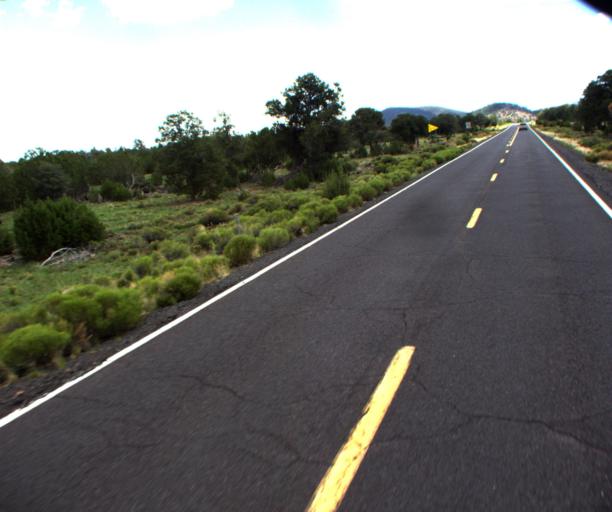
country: US
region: Arizona
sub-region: Coconino County
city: Parks
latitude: 35.5294
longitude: -111.8456
